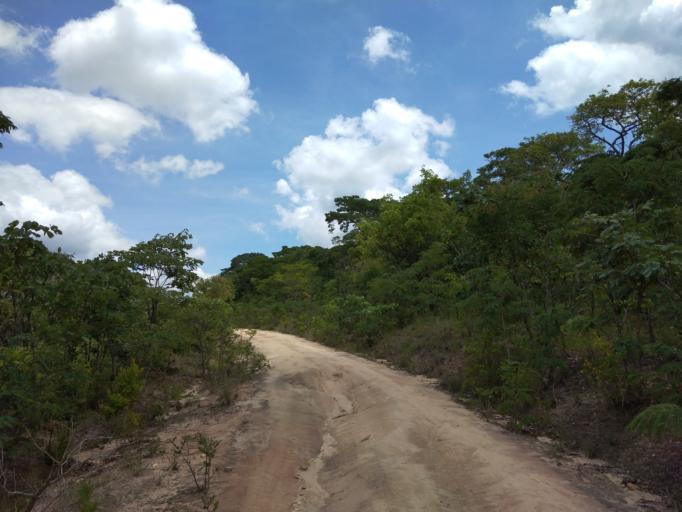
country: ZM
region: Central
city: Mkushi
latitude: -13.9800
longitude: 29.9407
